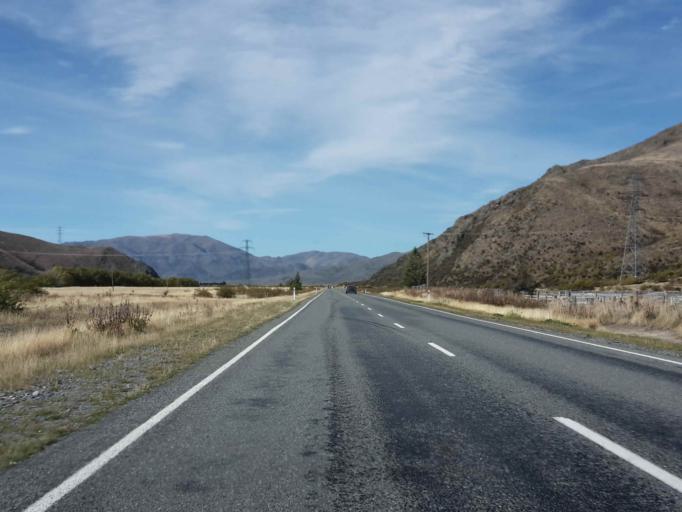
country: NZ
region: Otago
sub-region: Queenstown-Lakes District
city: Wanaka
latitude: -44.5001
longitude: 169.7659
